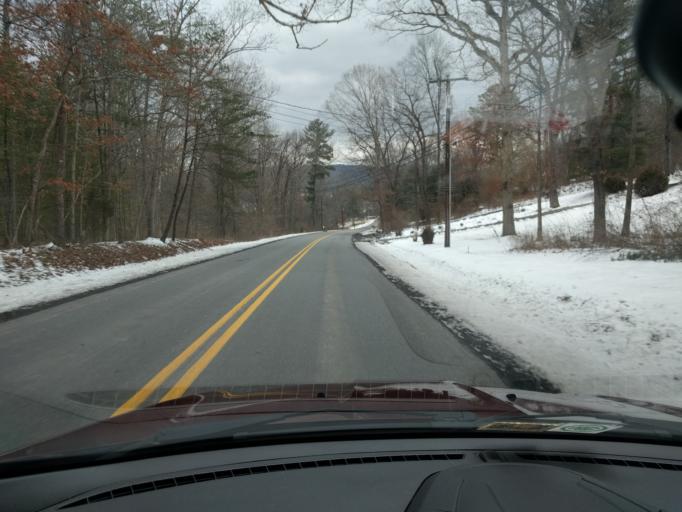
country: US
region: Virginia
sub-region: Alleghany County
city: Clifton Forge
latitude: 37.8274
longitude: -79.7751
